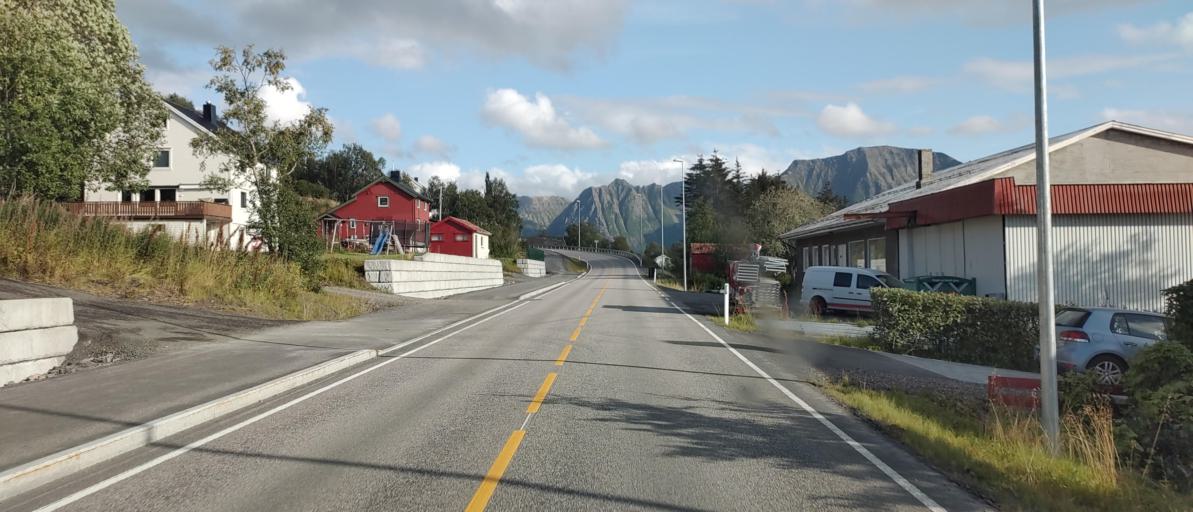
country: NO
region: Nordland
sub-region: Sortland
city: Sortland
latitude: 68.7526
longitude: 15.4728
